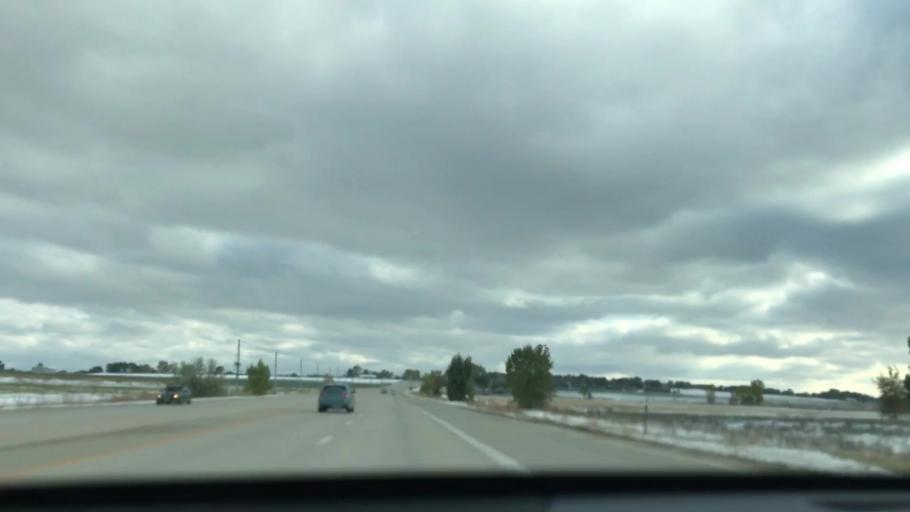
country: US
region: Colorado
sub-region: Boulder County
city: Lafayette
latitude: 40.0346
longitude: -105.1031
